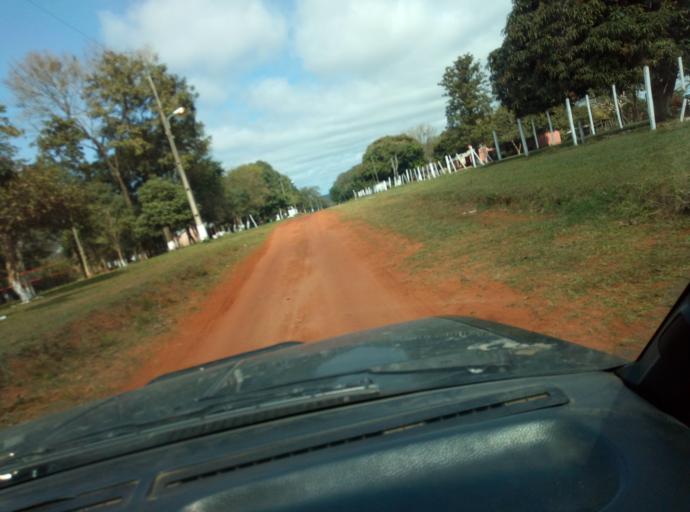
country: PY
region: Caaguazu
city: Doctor Cecilio Baez
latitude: -25.1567
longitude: -56.2916
